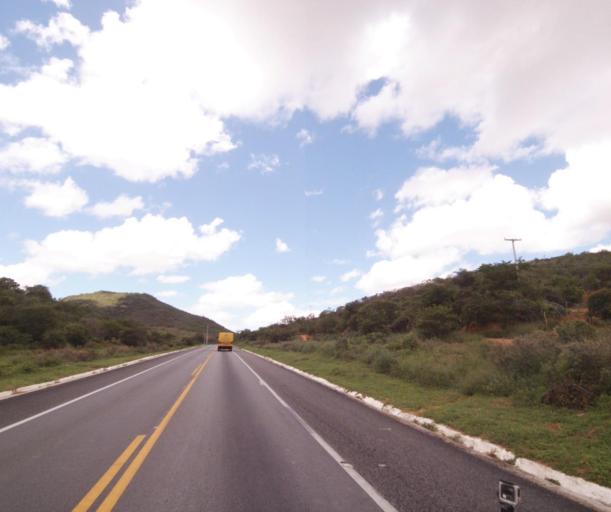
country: BR
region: Bahia
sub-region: Pocoes
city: Pocoes
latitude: -14.3560
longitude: -40.3369
